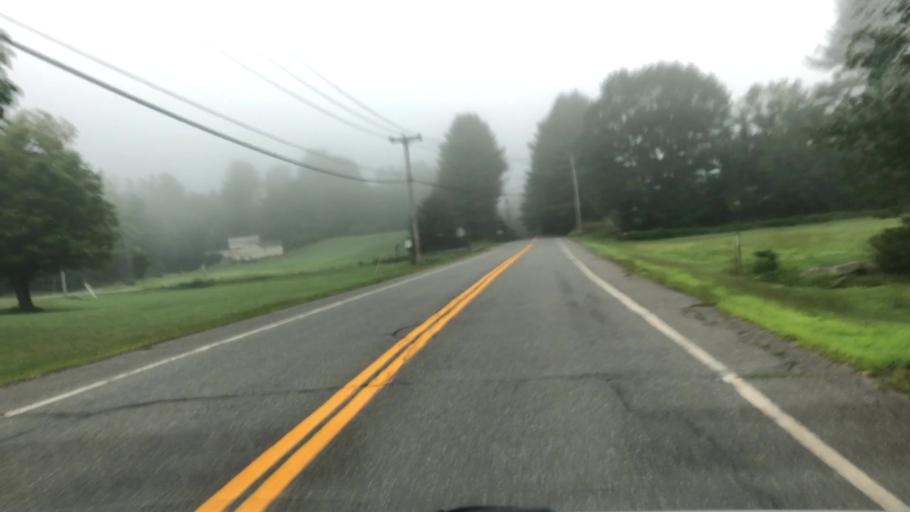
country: US
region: Massachusetts
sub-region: Franklin County
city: Shelburne Falls
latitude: 42.6136
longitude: -72.7613
